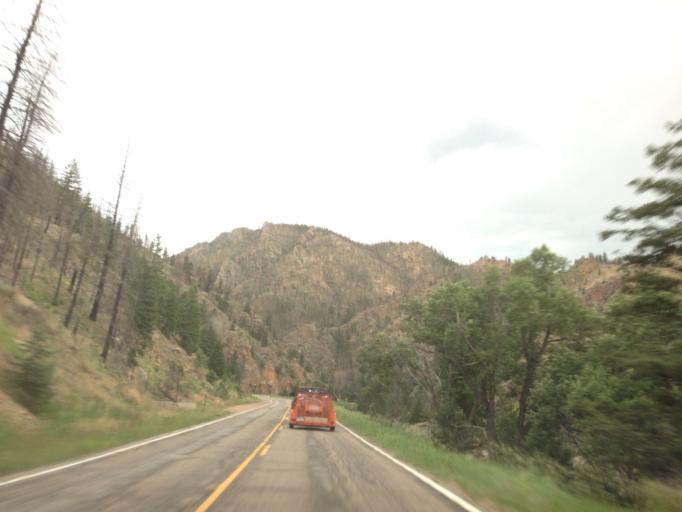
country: US
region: Colorado
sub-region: Larimer County
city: Laporte
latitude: 40.6855
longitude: -105.4337
